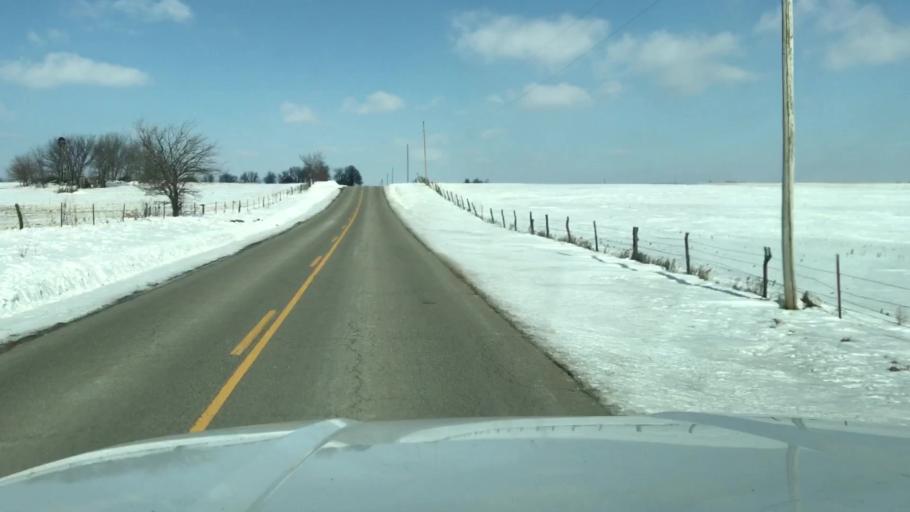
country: US
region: Missouri
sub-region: Nodaway County
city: Maryville
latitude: 40.3520
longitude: -94.7222
